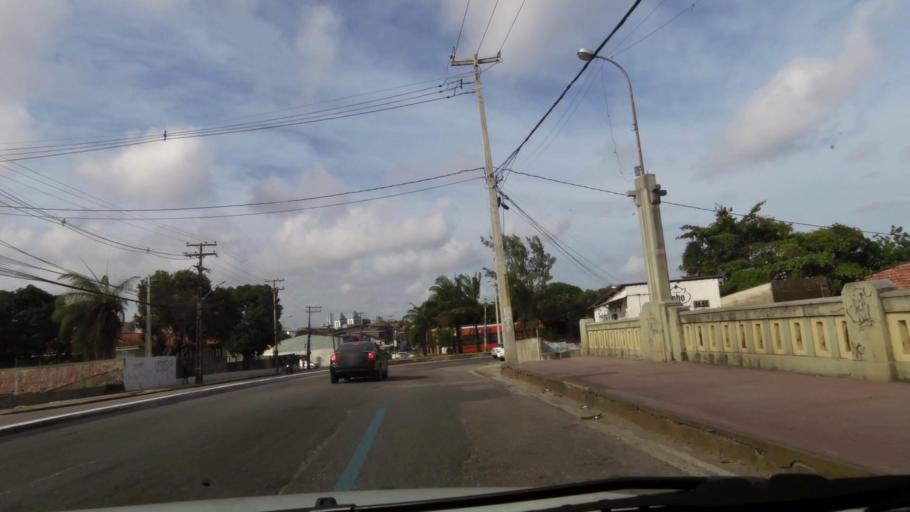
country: BR
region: Pernambuco
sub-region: Recife
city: Recife
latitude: -8.0814
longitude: -34.9053
